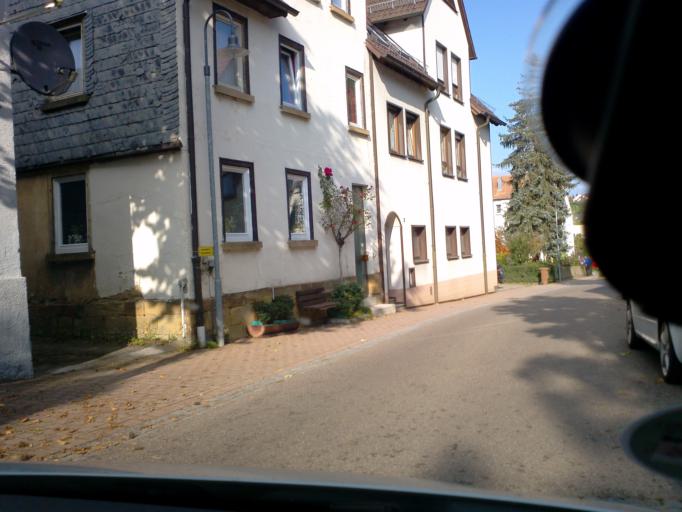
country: DE
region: Baden-Wuerttemberg
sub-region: Regierungsbezirk Stuttgart
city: Brackenheim
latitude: 49.0799
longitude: 9.0648
